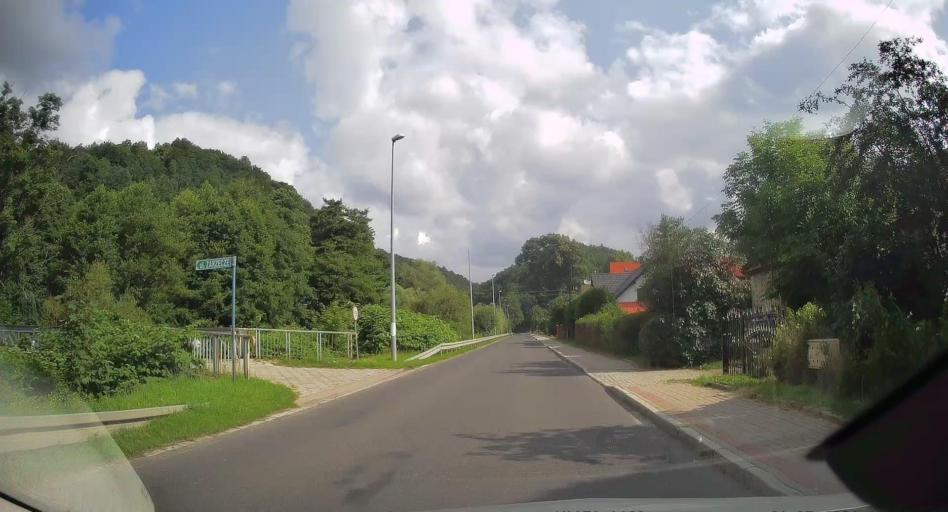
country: PL
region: Lower Silesian Voivodeship
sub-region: Powiat walbrzyski
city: Walim
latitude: 50.7335
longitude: 16.4036
